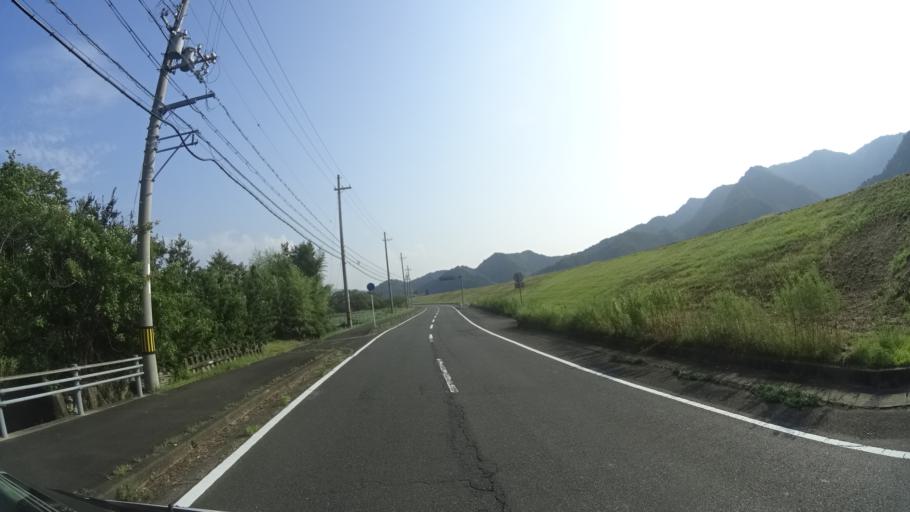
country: JP
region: Kyoto
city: Maizuru
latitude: 35.4789
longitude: 135.2833
